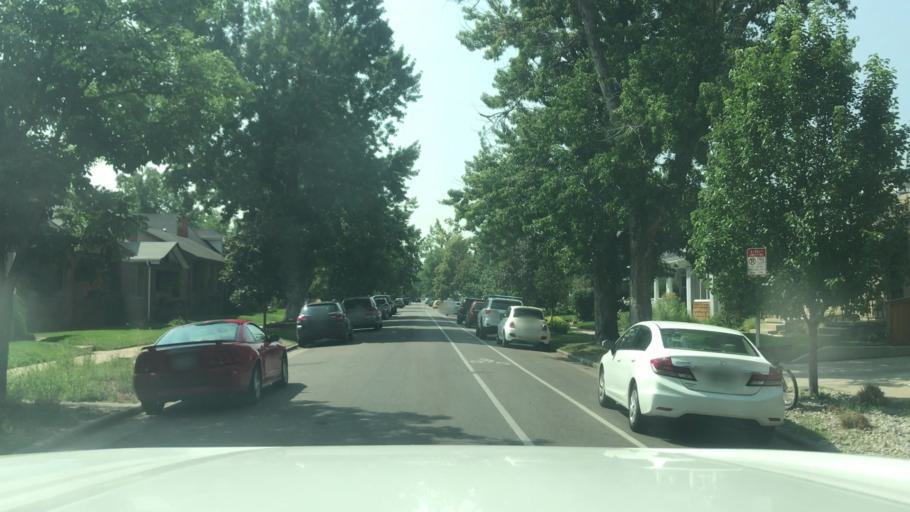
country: US
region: Colorado
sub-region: Denver County
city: Denver
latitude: 39.6995
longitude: -104.9793
